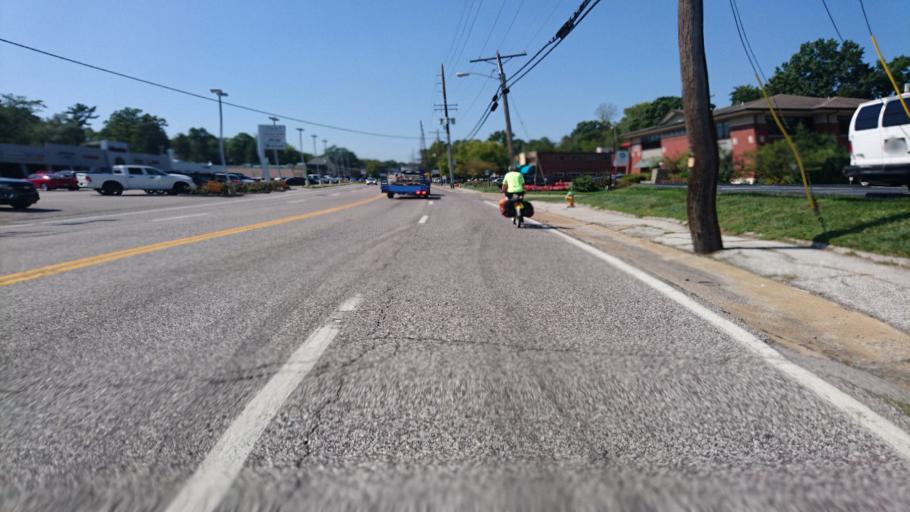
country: US
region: Missouri
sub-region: Saint Louis County
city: Warson Woods
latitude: 38.6025
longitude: -90.3886
